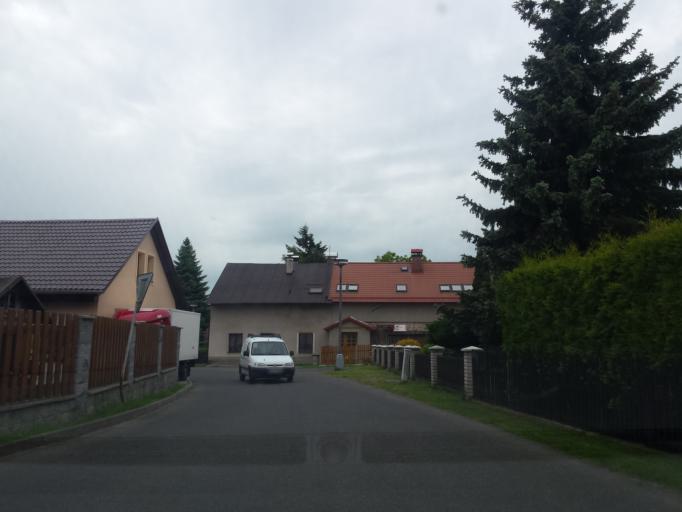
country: CZ
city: Novy Bor
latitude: 50.7664
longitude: 14.5518
